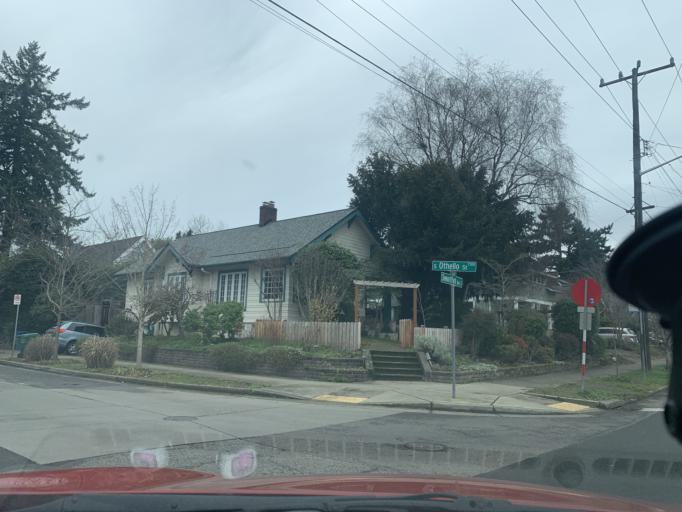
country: US
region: Washington
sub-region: King County
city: Bryn Mawr-Skyway
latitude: 47.5370
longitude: -122.2673
